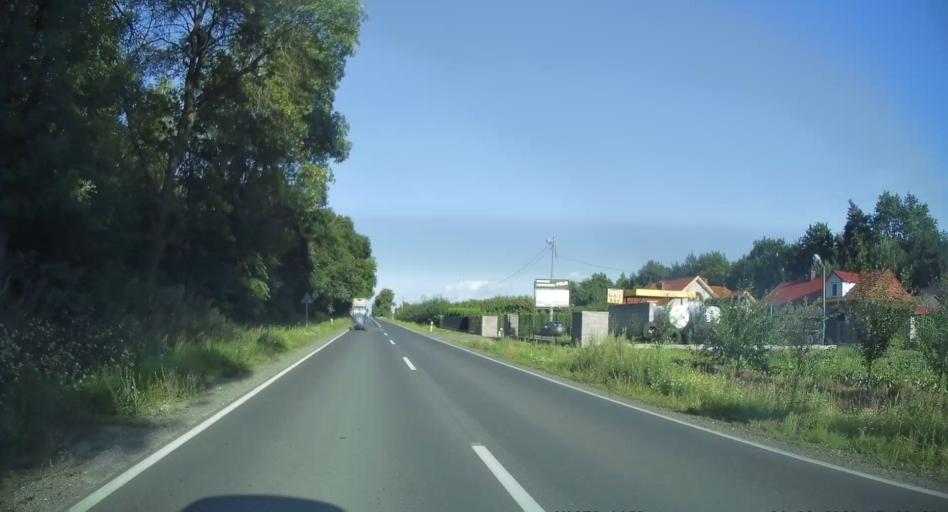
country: PL
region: Masovian Voivodeship
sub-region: Powiat grojecki
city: Bledow
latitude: 51.8041
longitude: 20.5923
